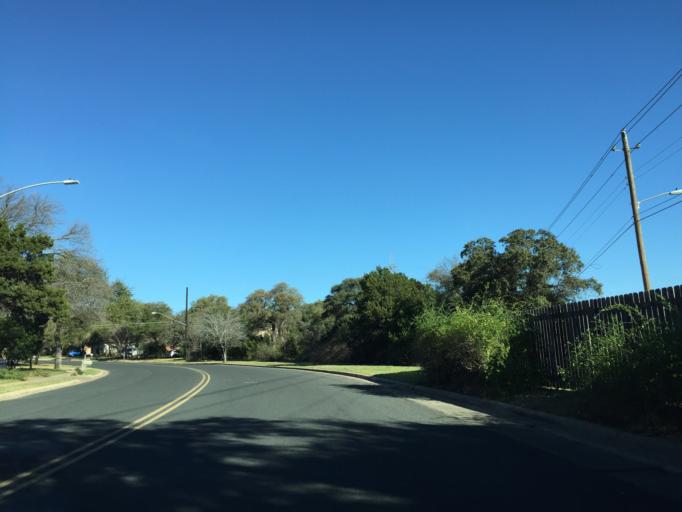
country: US
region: Texas
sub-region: Williamson County
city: Jollyville
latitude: 30.4040
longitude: -97.7290
